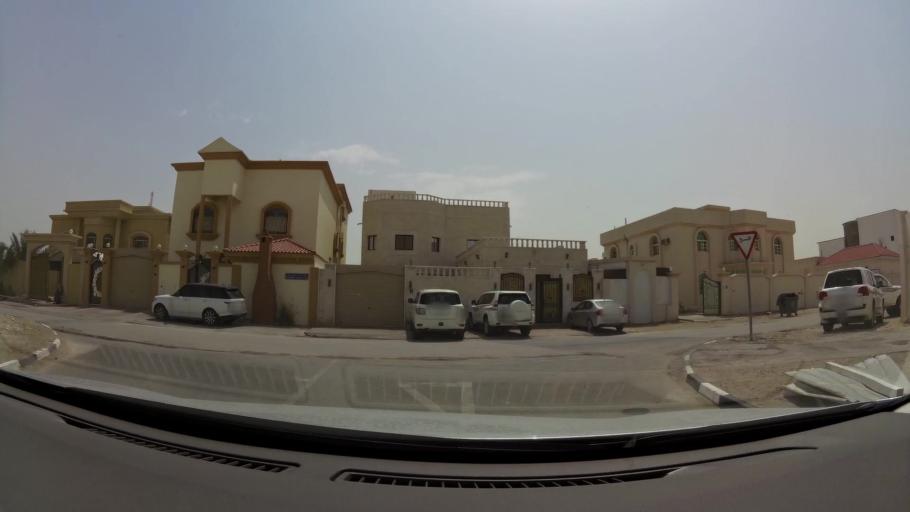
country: QA
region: Baladiyat ar Rayyan
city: Ar Rayyan
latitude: 25.2289
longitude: 51.4148
